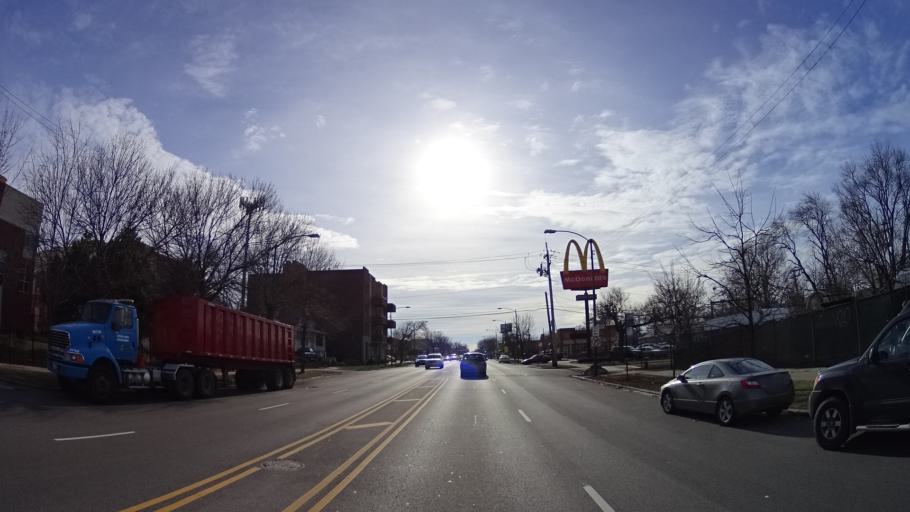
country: US
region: Illinois
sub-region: Cook County
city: Evanston
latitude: 42.0082
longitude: -87.6902
